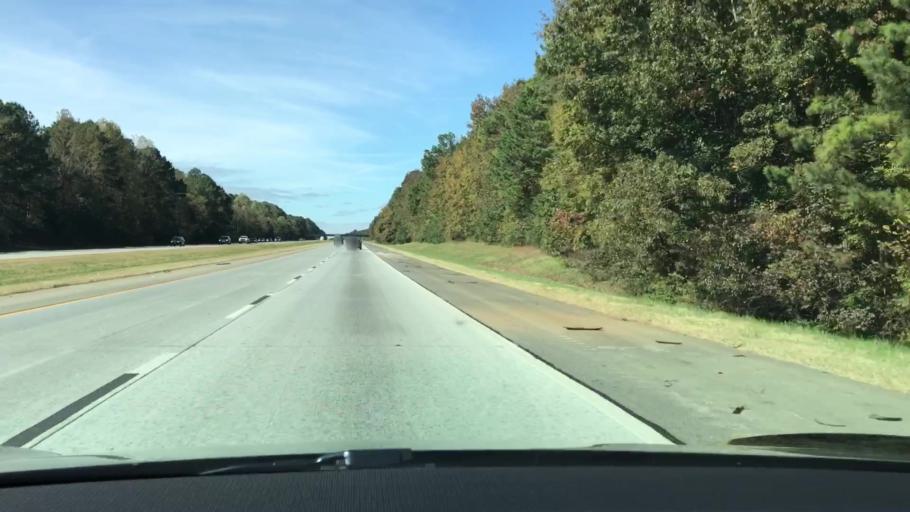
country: US
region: Georgia
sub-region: Morgan County
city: Madison
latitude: 33.5548
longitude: -83.4224
